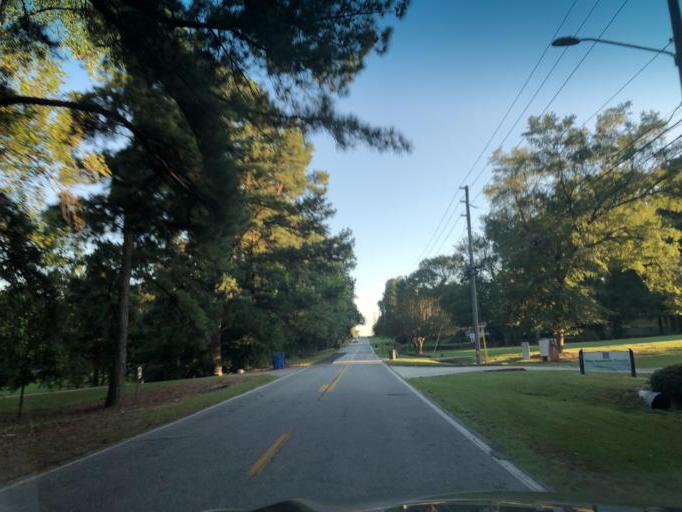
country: US
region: Georgia
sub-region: Muscogee County
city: Columbus
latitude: 32.5291
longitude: -84.8916
